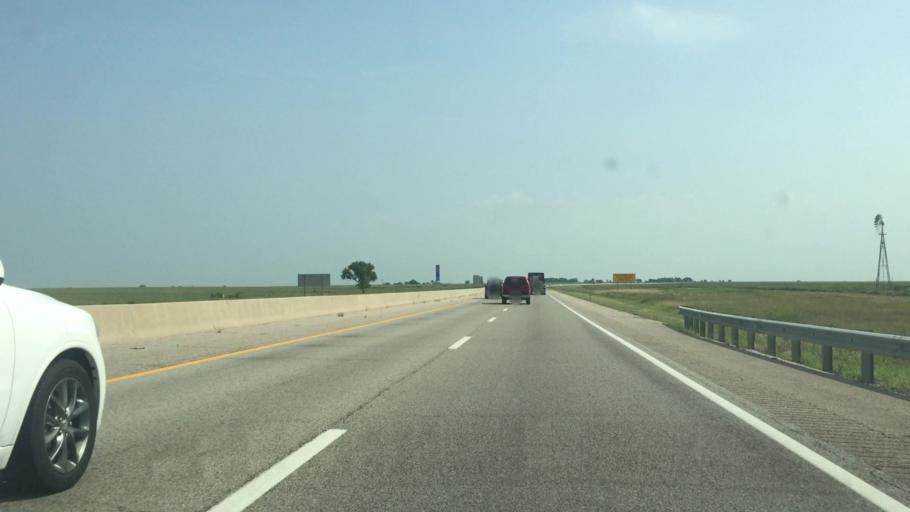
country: US
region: Kansas
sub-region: Butler County
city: El Dorado
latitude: 37.8901
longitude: -96.8378
